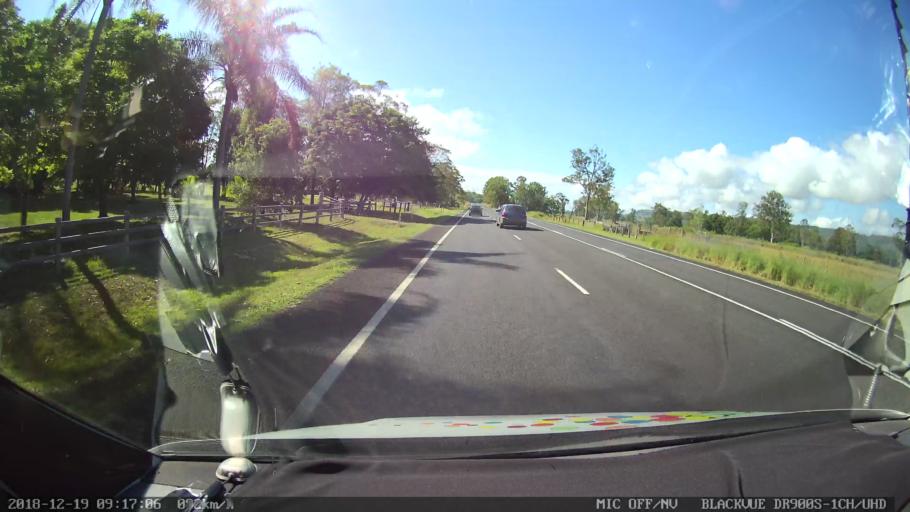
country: AU
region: New South Wales
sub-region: Kyogle
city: Kyogle
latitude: -28.5290
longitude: 152.9724
